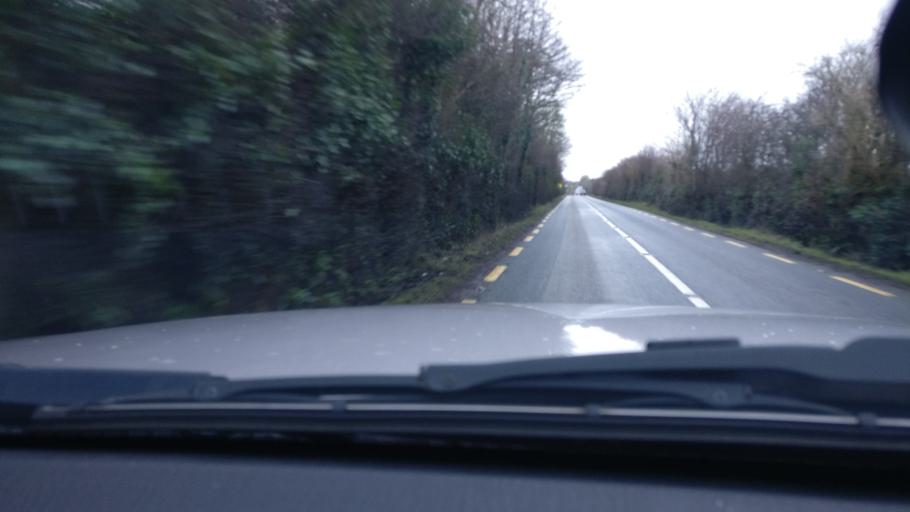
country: IE
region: Leinster
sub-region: An Iarmhi
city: Moate
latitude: 53.5815
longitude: -7.7328
